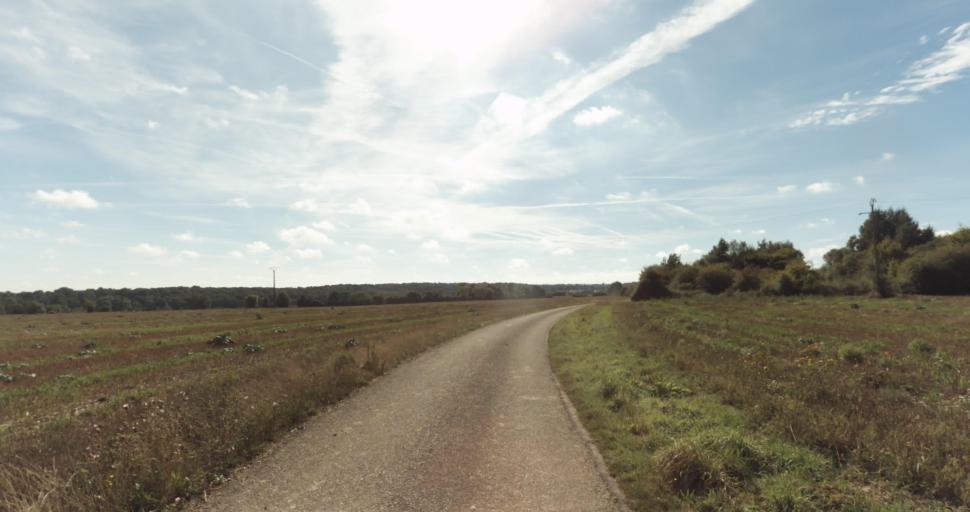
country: FR
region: Lower Normandy
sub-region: Departement du Calvados
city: Orbec
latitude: 48.9399
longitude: 0.3575
